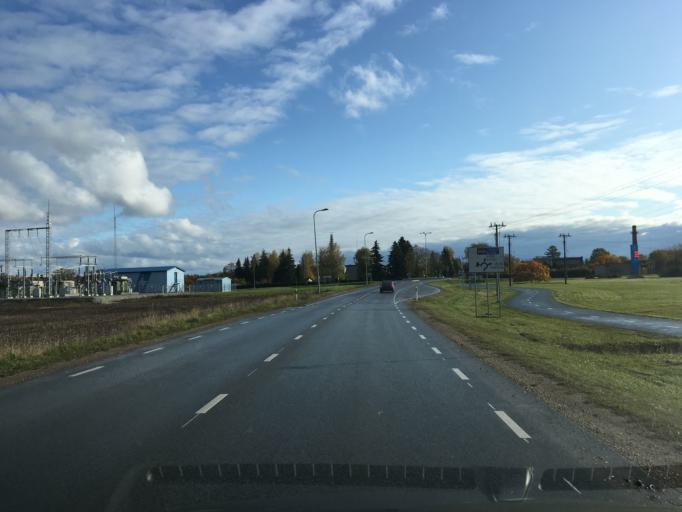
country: EE
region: Harju
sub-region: Raasiku vald
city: Raasiku
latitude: 59.1871
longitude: 25.1563
